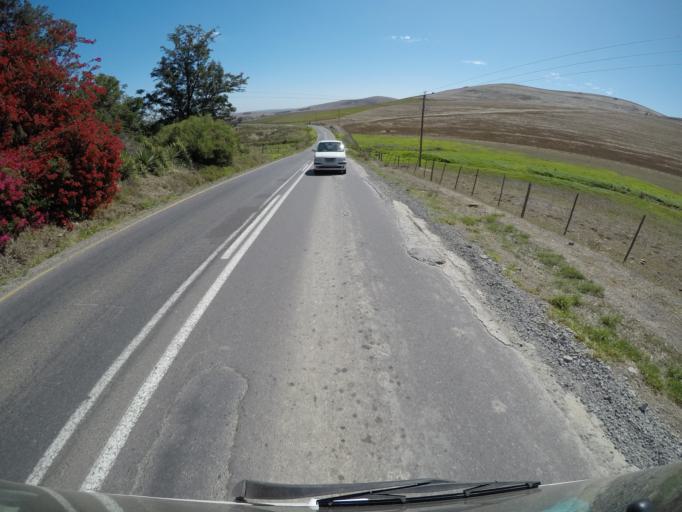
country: ZA
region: Western Cape
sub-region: City of Cape Town
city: Kraaifontein
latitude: -33.7927
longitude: 18.6034
